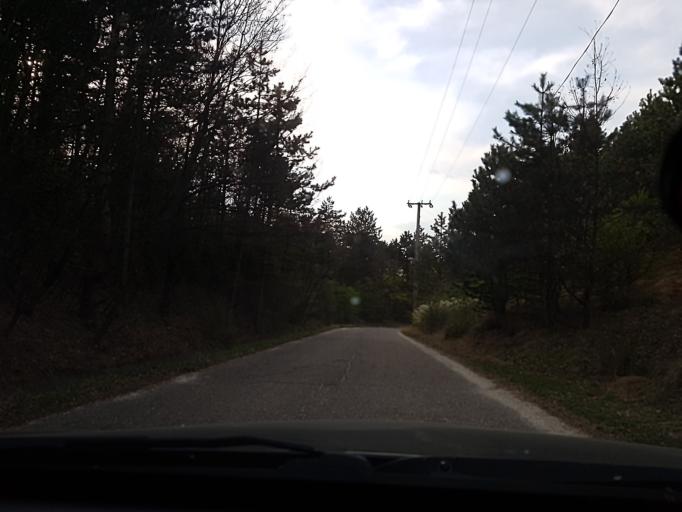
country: HU
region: Pest
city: Piliscsaba
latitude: 47.6295
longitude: 18.8355
